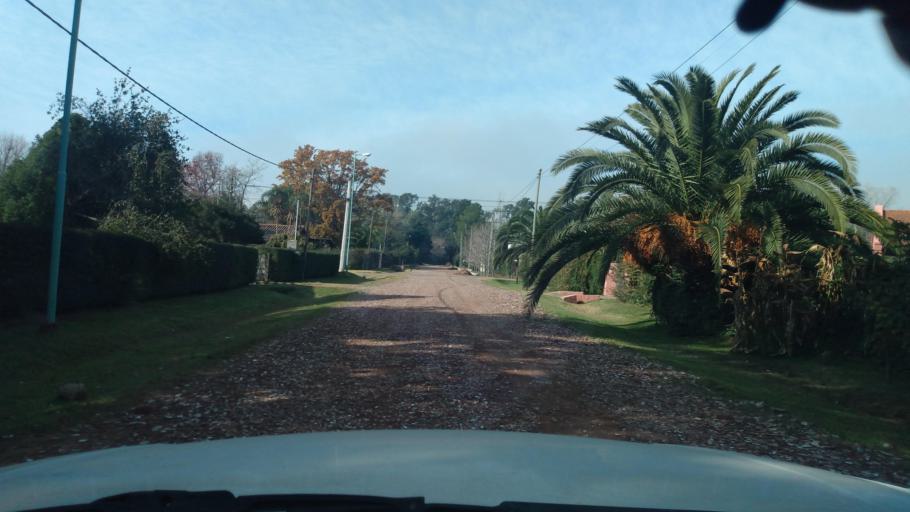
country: AR
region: Buenos Aires
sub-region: Partido de Lujan
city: Lujan
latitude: -34.5926
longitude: -59.1392
